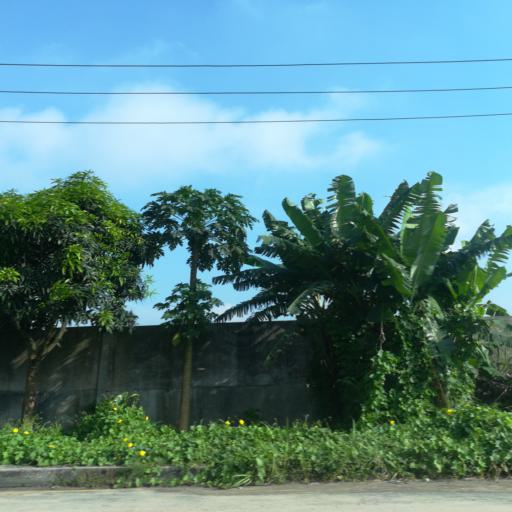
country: NG
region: Rivers
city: Port Harcourt
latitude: 4.8015
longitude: 7.0249
